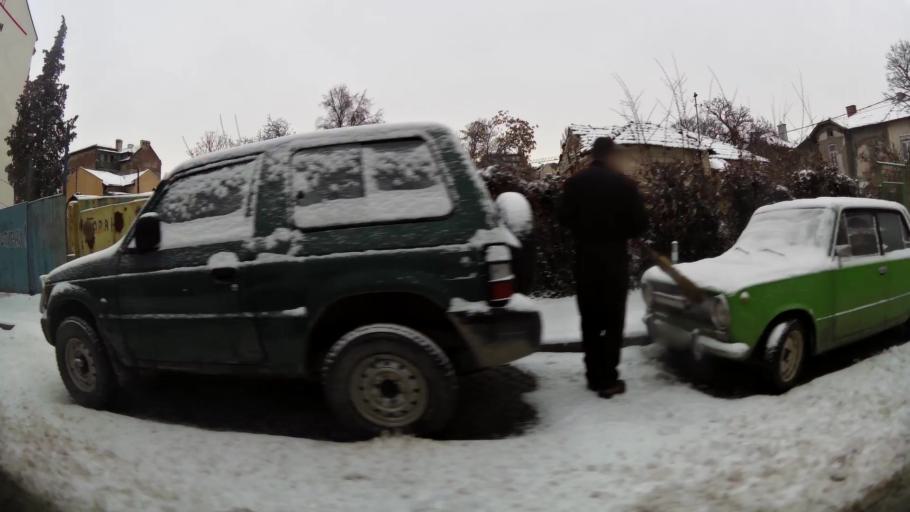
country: BG
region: Sofia-Capital
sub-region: Stolichna Obshtina
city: Sofia
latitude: 42.7052
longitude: 23.3094
